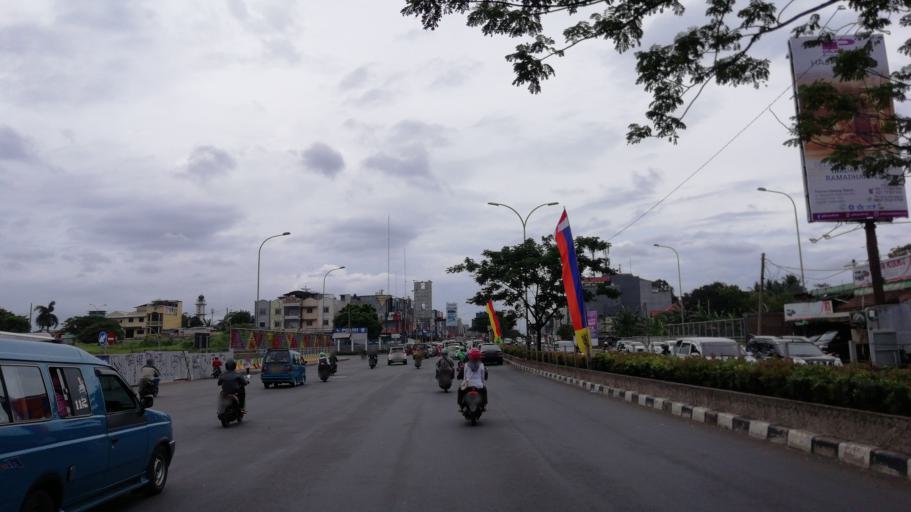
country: ID
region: West Java
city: Depok
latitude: -6.3755
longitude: 106.8323
